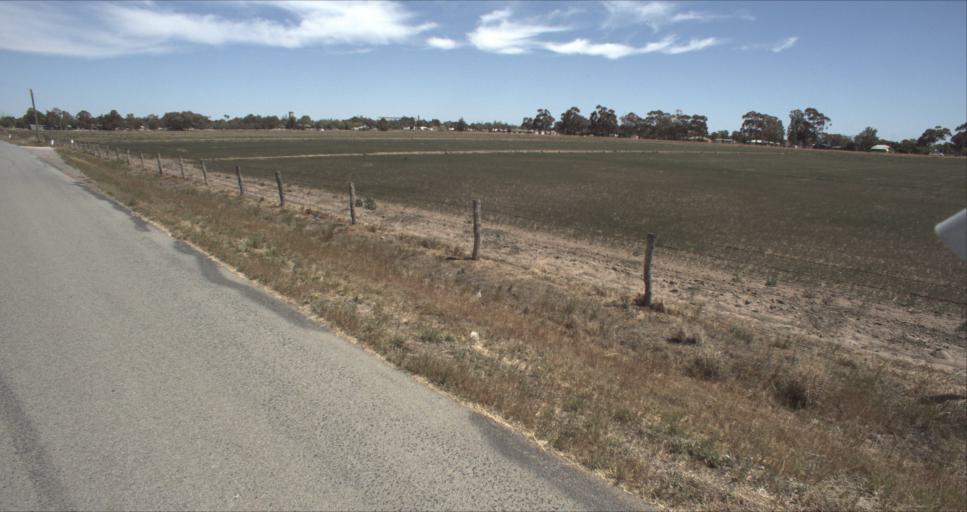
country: AU
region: New South Wales
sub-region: Leeton
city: Leeton
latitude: -34.5959
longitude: 146.4165
